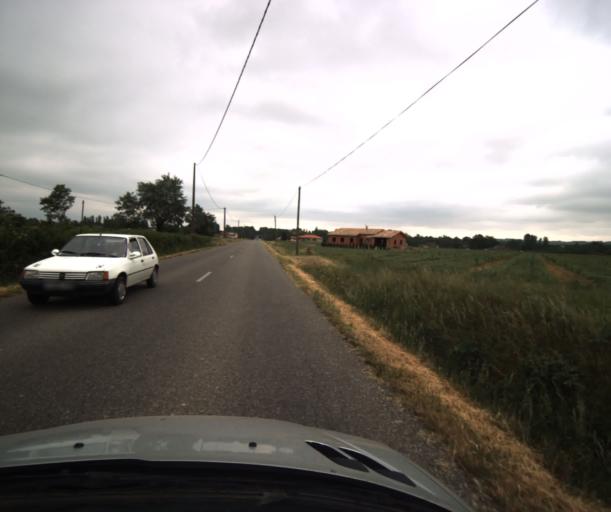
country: FR
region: Midi-Pyrenees
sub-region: Departement du Tarn-et-Garonne
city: Saint-Nicolas-de-la-Grave
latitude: 44.0323
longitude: 1.0298
